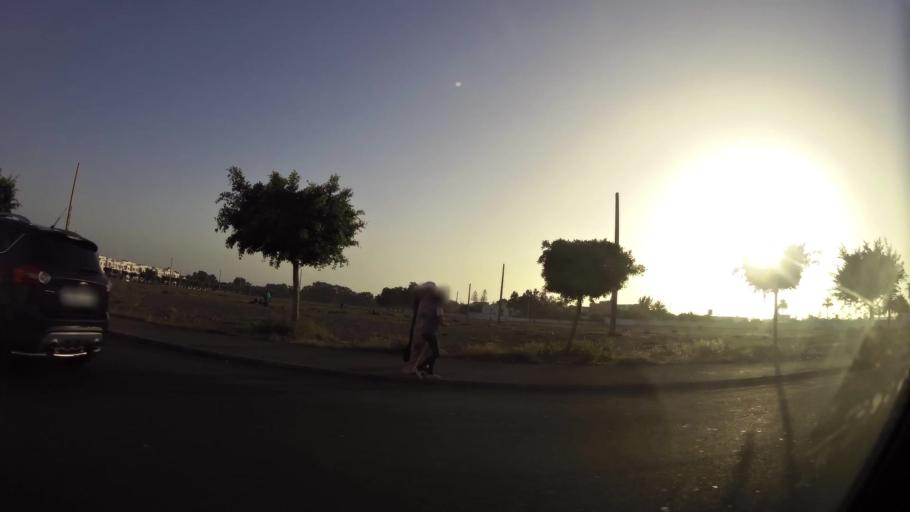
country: MA
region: Oued ed Dahab-Lagouira
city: Dakhla
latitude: 30.3938
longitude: -9.5730
